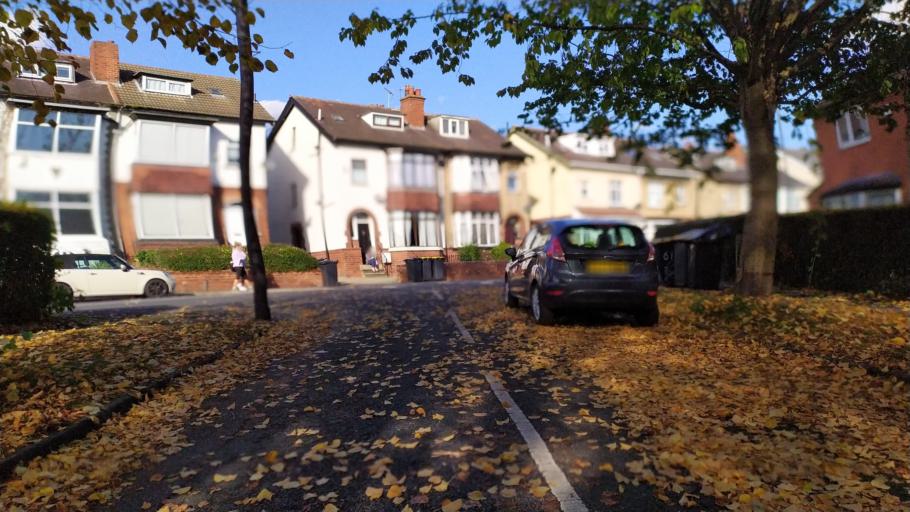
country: GB
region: England
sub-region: City and Borough of Leeds
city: Leeds
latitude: 53.8198
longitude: -1.5875
